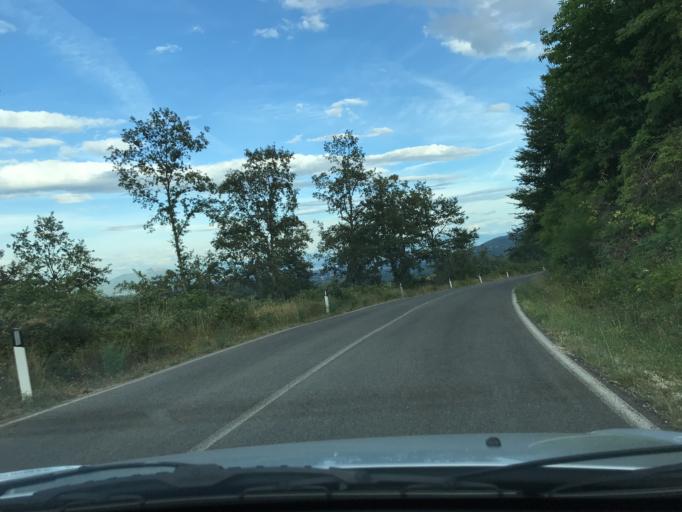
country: IT
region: Umbria
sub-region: Provincia di Terni
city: Guardea
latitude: 42.6523
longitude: 12.3516
